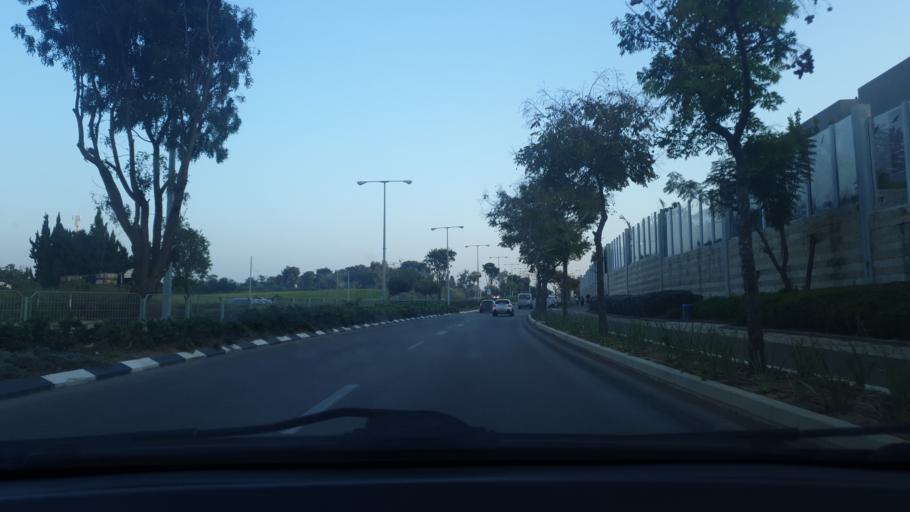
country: IL
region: Central District
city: Bet Dagan
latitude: 31.9701
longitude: 34.8254
